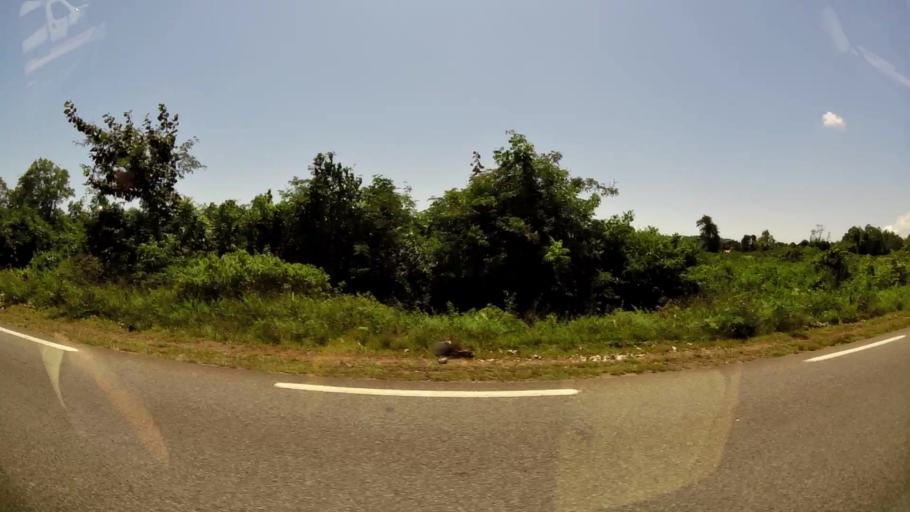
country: GF
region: Guyane
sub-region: Guyane
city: Cayenne
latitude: 4.9167
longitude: -52.3308
